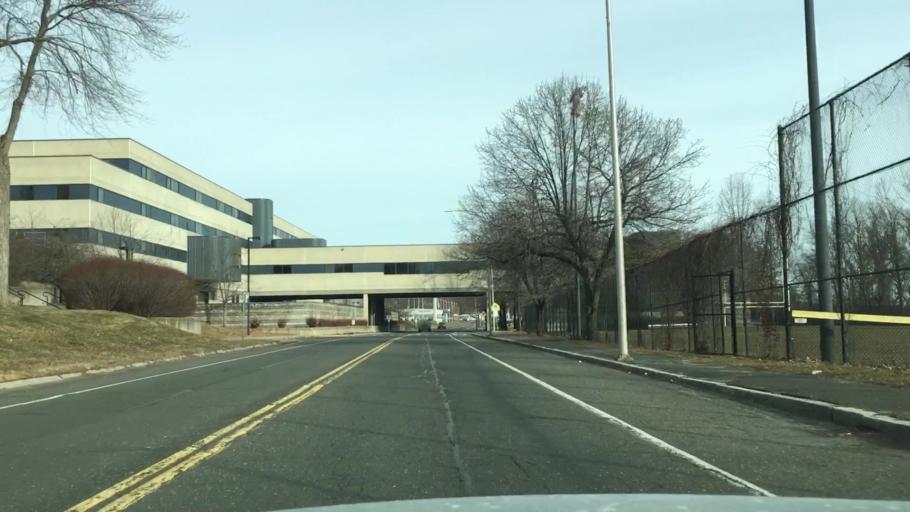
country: US
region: Massachusetts
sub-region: Hampden County
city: Holyoke
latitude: 42.1774
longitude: -72.6300
